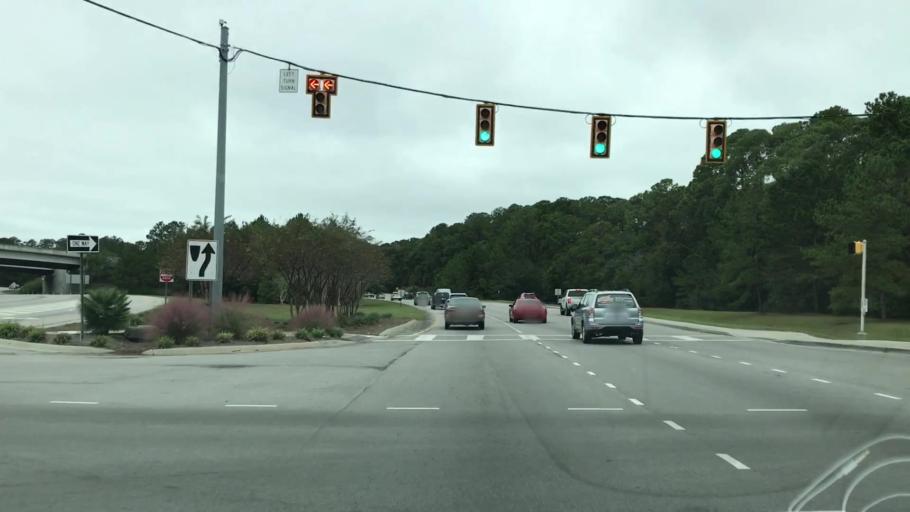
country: US
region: South Carolina
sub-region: Beaufort County
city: Hilton Head Island
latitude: 32.2162
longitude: -80.7379
